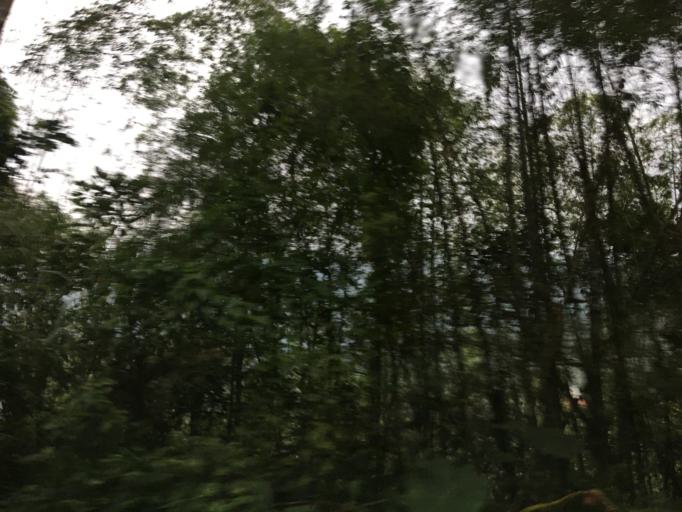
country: TW
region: Taiwan
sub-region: Chiayi
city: Jiayi Shi
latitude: 23.5385
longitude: 120.6274
